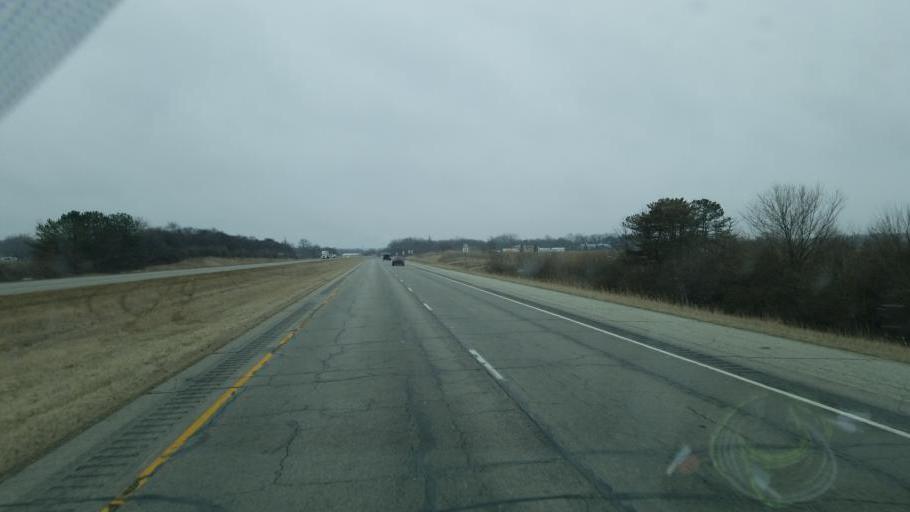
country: US
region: Indiana
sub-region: Wabash County
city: Wabash
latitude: 40.8002
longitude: -85.8744
